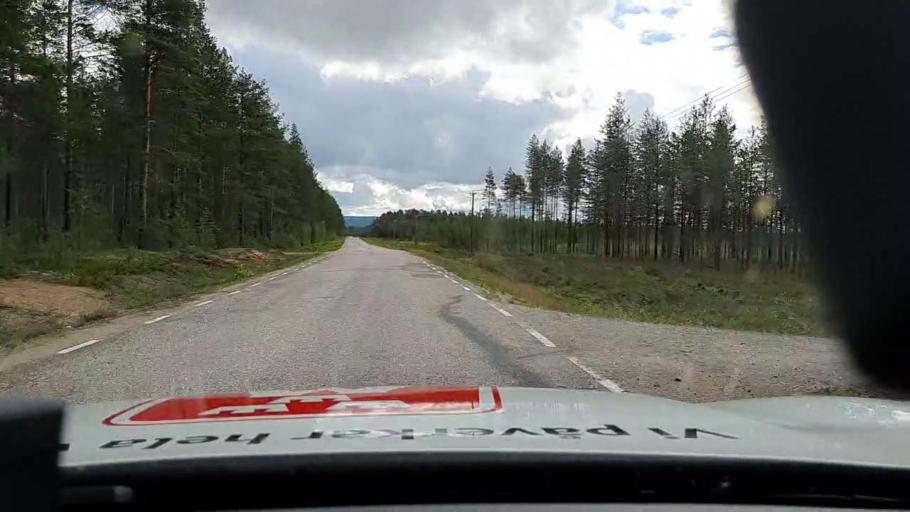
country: SE
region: Norrbotten
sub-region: Overkalix Kommun
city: OEverkalix
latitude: 66.2496
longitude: 22.8848
